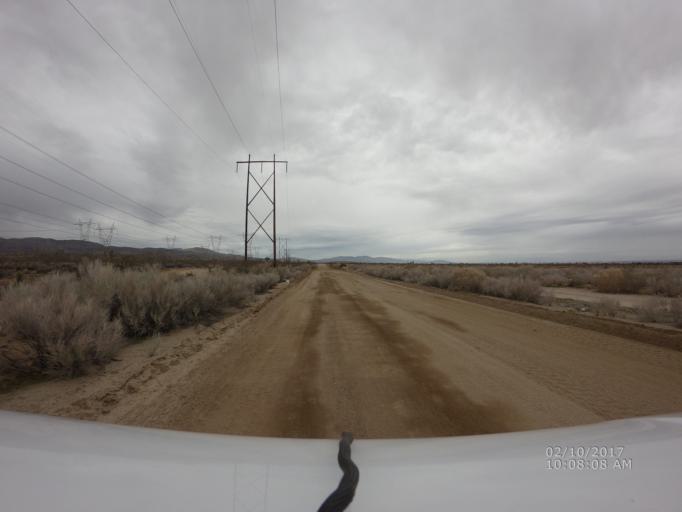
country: US
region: California
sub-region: Los Angeles County
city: Littlerock
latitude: 34.5139
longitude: -117.9509
